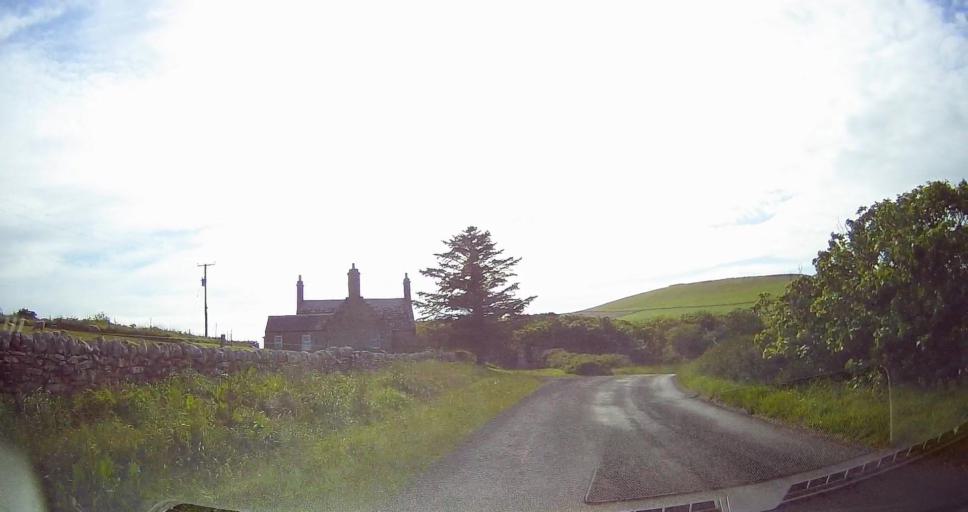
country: GB
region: Scotland
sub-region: Orkney Islands
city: Stromness
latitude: 58.7854
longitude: -3.2555
